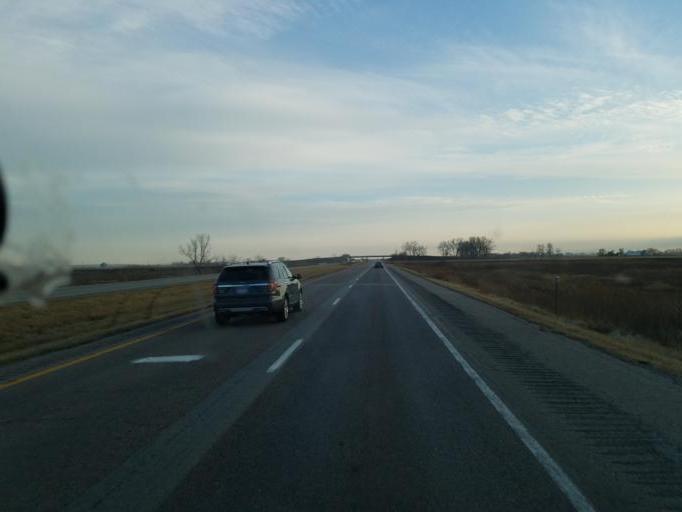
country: US
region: Nebraska
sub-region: Washington County
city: Blair
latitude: 41.6740
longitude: -96.0376
